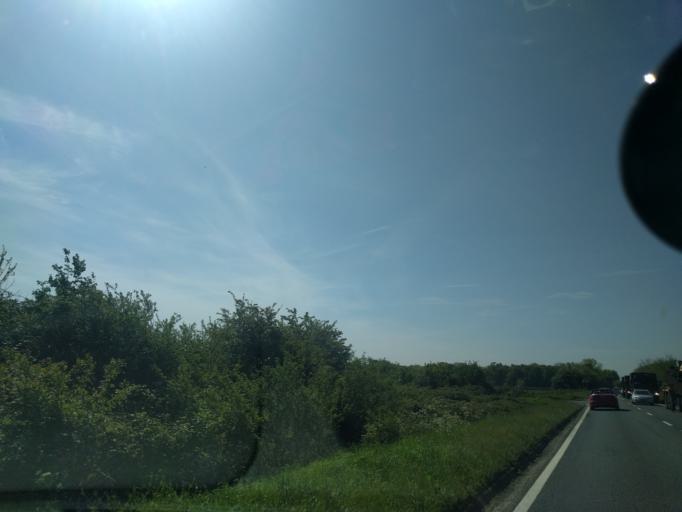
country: GB
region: England
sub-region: Somerset
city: Ilchester
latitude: 51.0273
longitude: -2.6626
